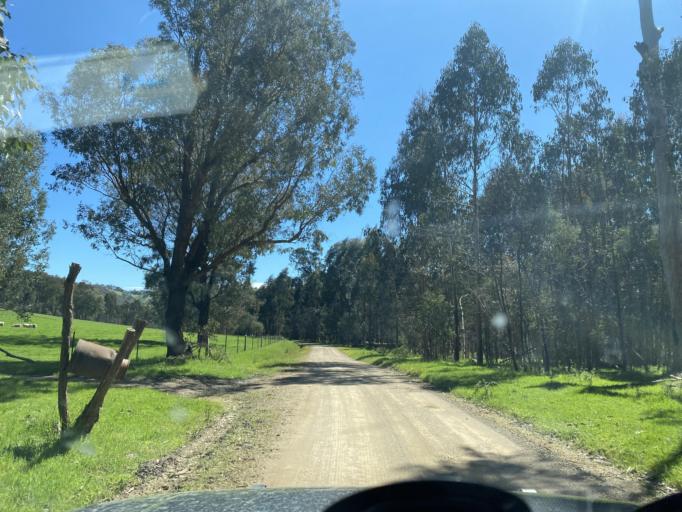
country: AU
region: Victoria
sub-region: Benalla
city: Benalla
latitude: -36.7013
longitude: 146.1789
